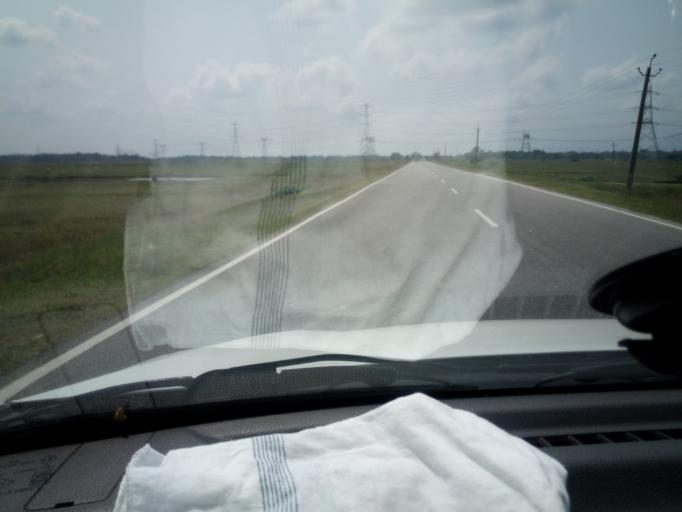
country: IN
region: Assam
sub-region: Udalguri
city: Udalguri
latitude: 26.7299
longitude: 92.1754
